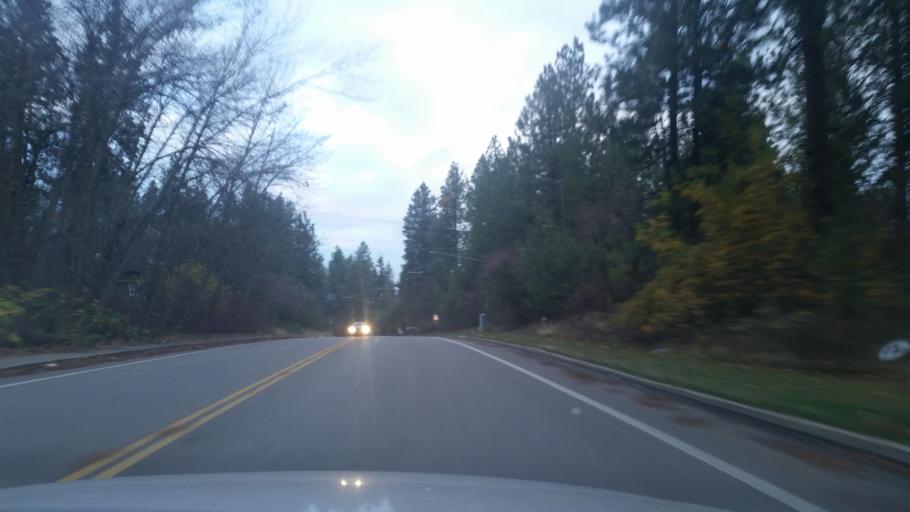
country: US
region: Washington
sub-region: Spokane County
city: Spokane
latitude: 47.6368
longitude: -117.3781
